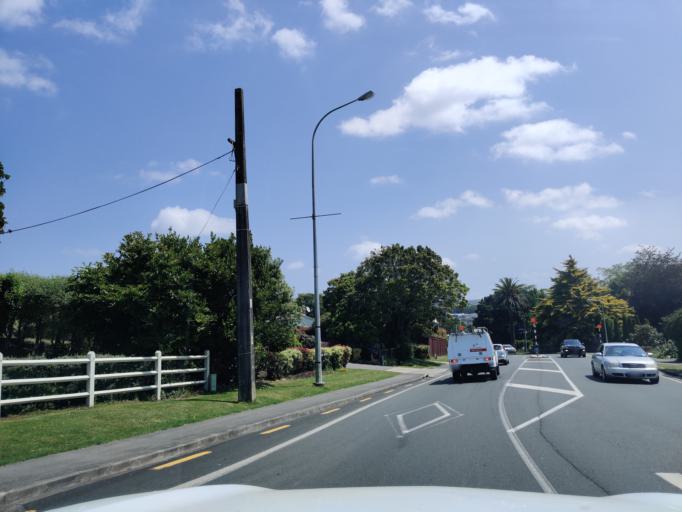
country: NZ
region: Auckland
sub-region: Auckland
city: Pukekohe East
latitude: -37.1995
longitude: 174.9103
